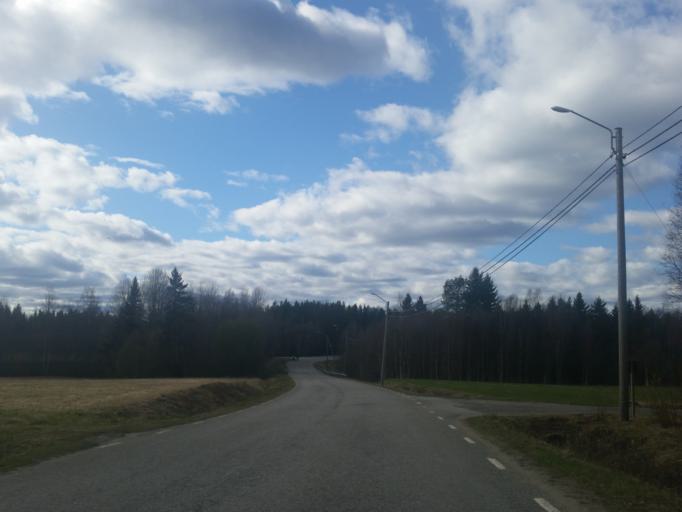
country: SE
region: Vaesterbotten
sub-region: Robertsfors Kommun
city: Robertsfors
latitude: 64.0458
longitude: 20.8563
